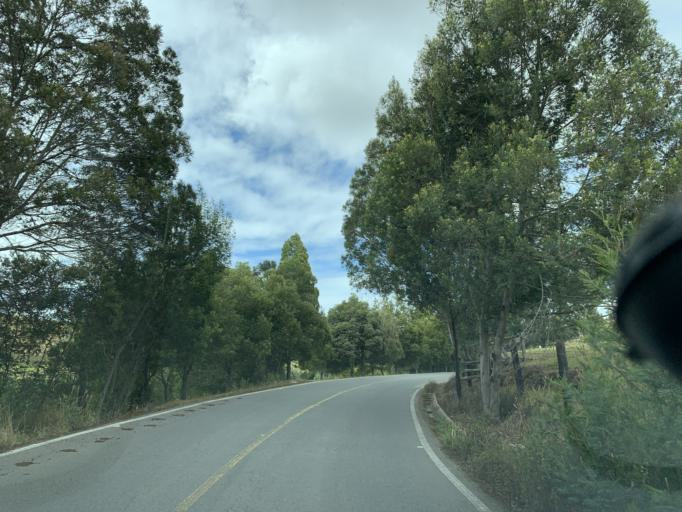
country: CO
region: Boyaca
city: Toca
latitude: 5.5698
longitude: -73.2380
